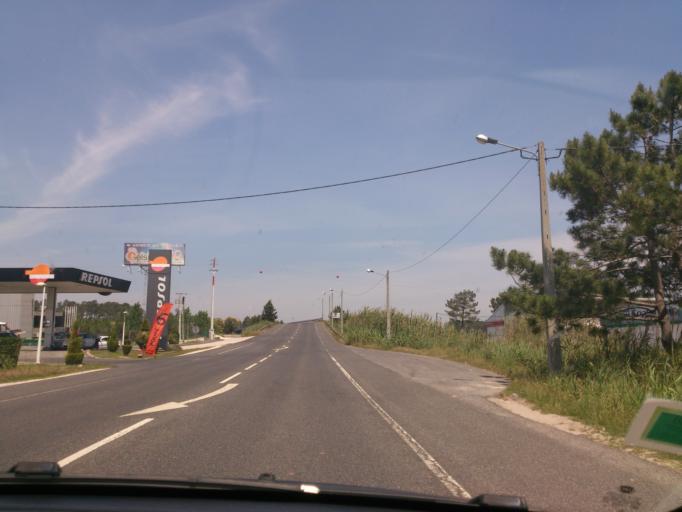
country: PT
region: Leiria
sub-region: Alcobaca
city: Alcobaca
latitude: 39.5830
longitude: -9.0120
